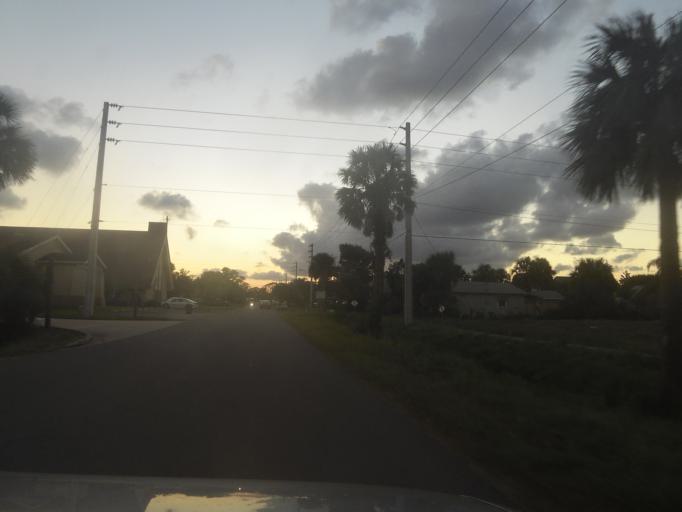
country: US
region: Florida
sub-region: Duval County
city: Jacksonville Beach
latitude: 30.2732
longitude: -81.3895
